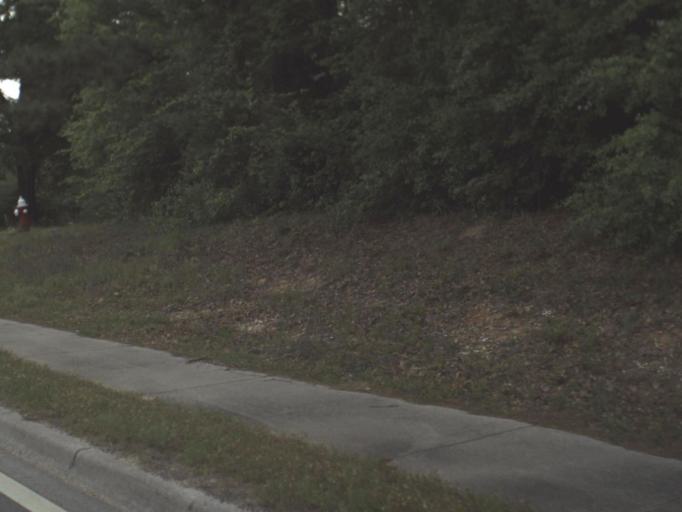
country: US
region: Florida
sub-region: Escambia County
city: Century
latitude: 30.9614
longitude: -87.2741
